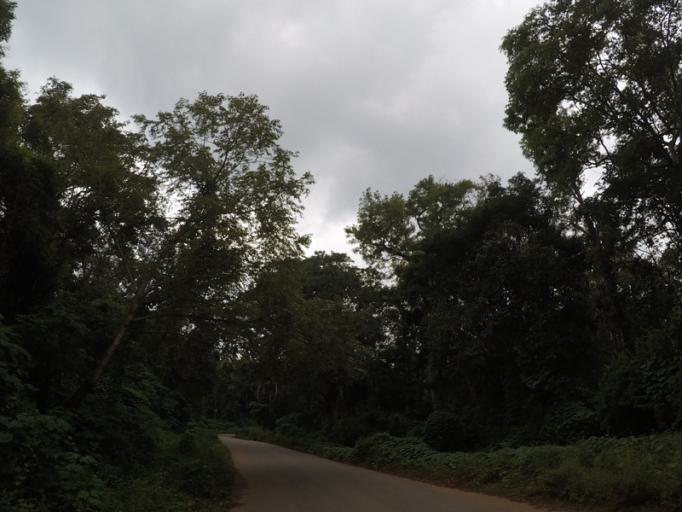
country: IN
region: Karnataka
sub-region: Chikmagalur
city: Chikmagalur
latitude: 13.4639
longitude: 75.7984
